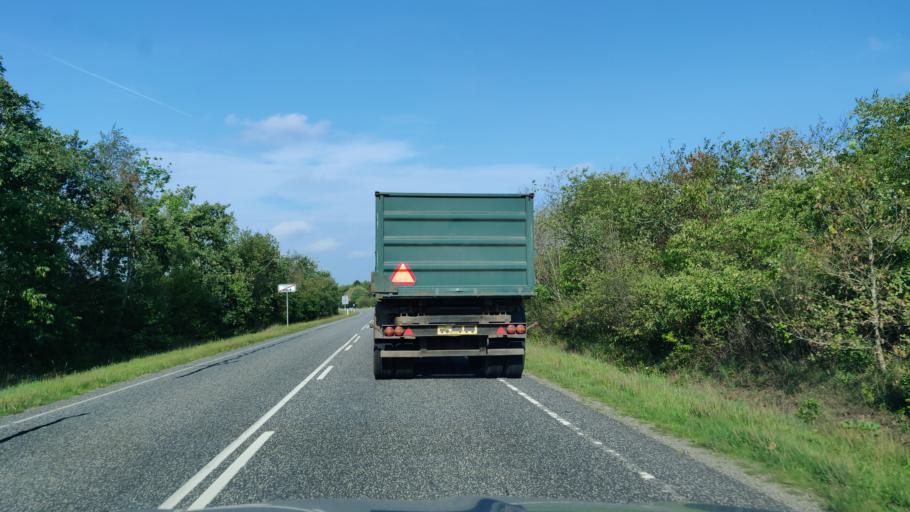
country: DK
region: Central Jutland
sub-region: Herning Kommune
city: Sunds
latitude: 56.2420
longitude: 9.0869
